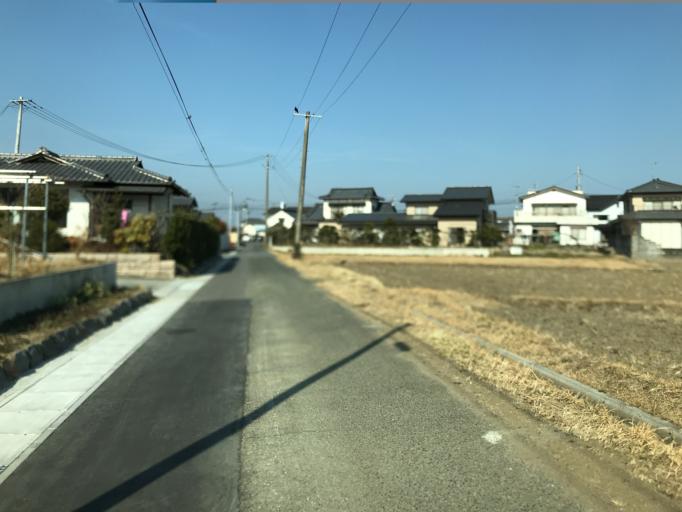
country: JP
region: Fukushima
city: Iwaki
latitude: 37.0530
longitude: 140.9506
